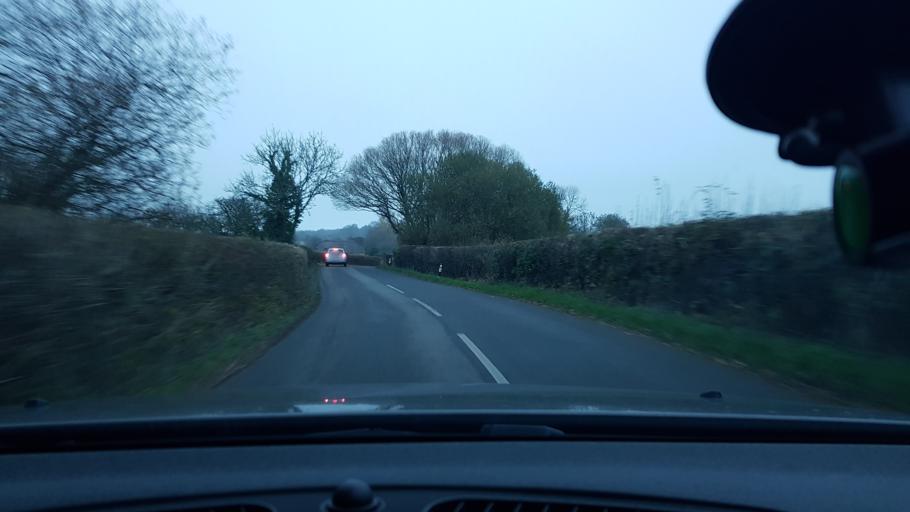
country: GB
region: England
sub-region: Dorset
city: Bovington Camp
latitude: 50.7438
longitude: -2.2751
